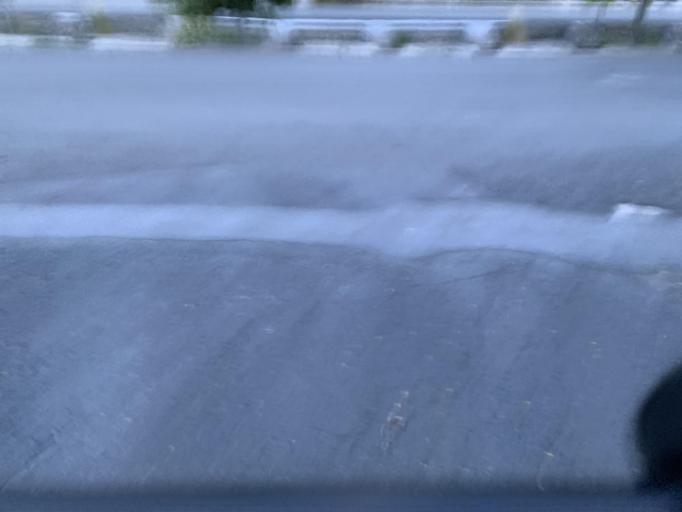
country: MX
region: Nuevo Leon
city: Santiago
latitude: 25.5088
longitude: -100.1874
